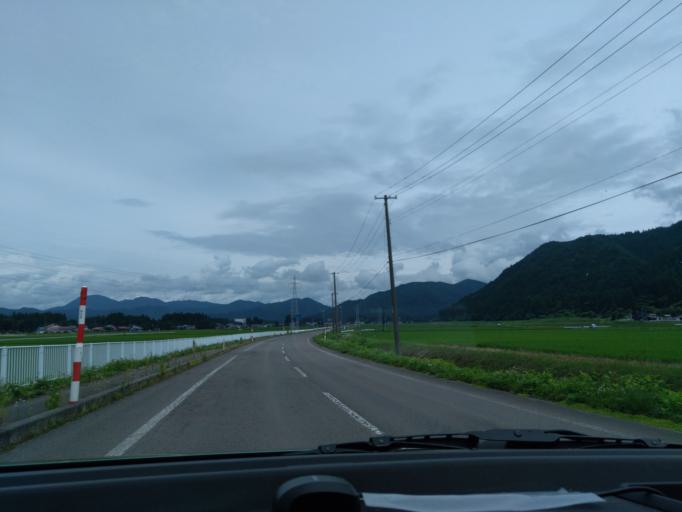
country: JP
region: Akita
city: Kakunodatemachi
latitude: 39.5940
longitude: 140.6145
